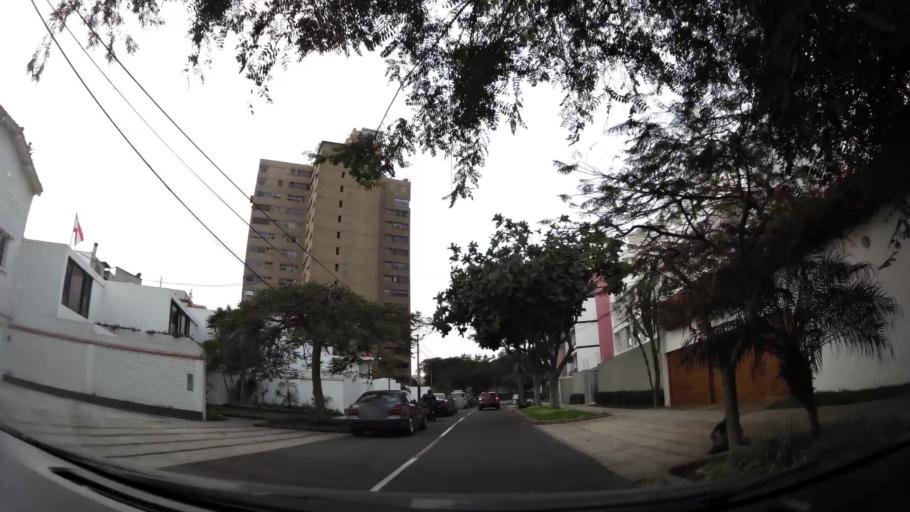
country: PE
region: Lima
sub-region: Lima
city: San Isidro
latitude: -12.1038
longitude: -77.0503
